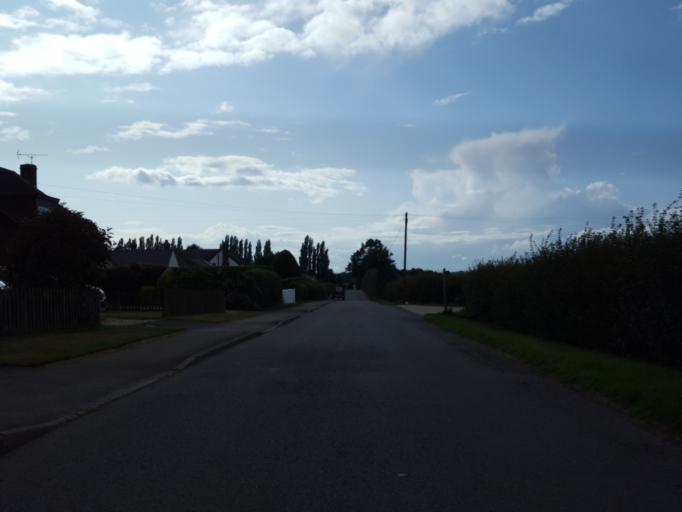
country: GB
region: England
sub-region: Kent
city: Maidstone
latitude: 51.2334
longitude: 0.5269
